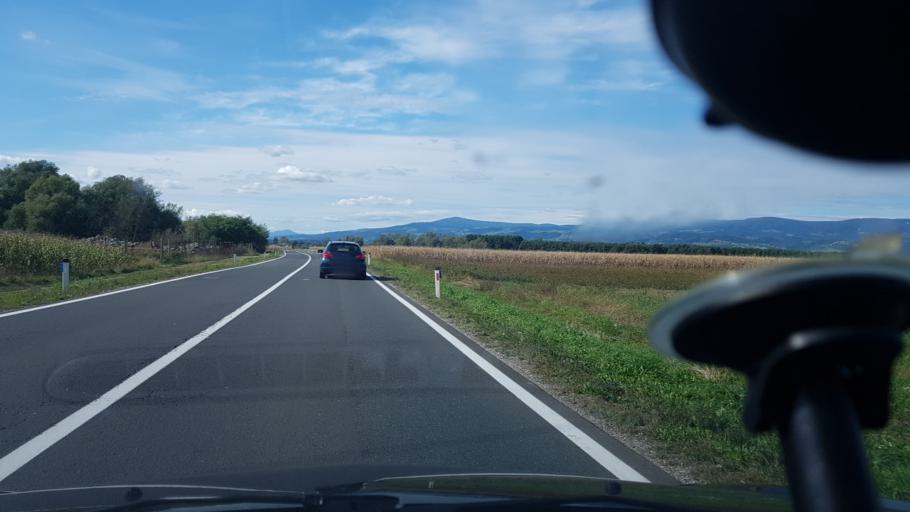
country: SI
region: Majsperk
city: Majsperk
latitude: 46.4091
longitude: 15.7259
